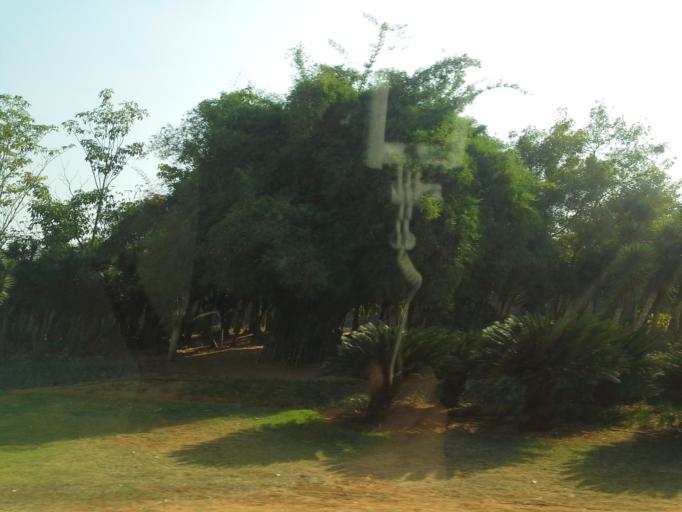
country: IN
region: Telangana
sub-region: Rangareddi
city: Balapur
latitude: 17.2444
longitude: 78.3910
